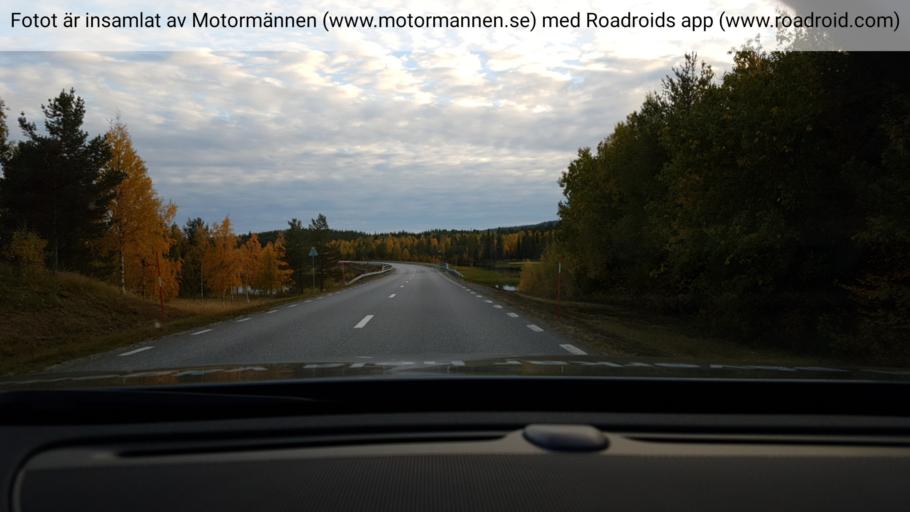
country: SE
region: Norrbotten
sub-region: Jokkmokks Kommun
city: Jokkmokk
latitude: 66.4300
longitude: 19.6850
